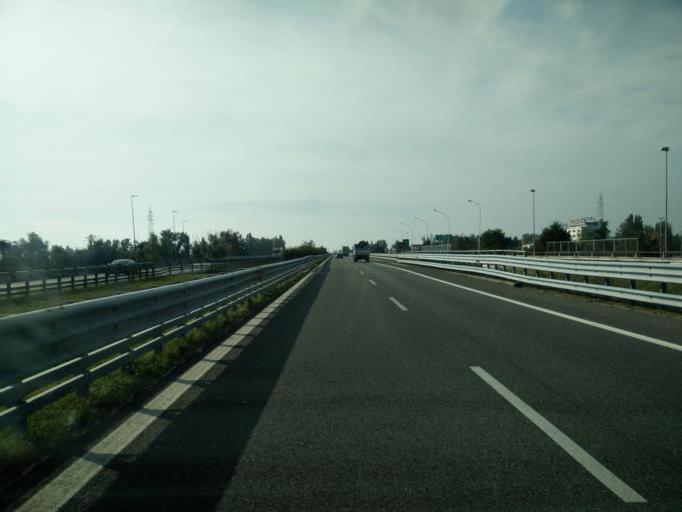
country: IT
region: Lombardy
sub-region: Provincia di Cremona
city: San Felice
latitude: 45.1430
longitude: 10.0717
